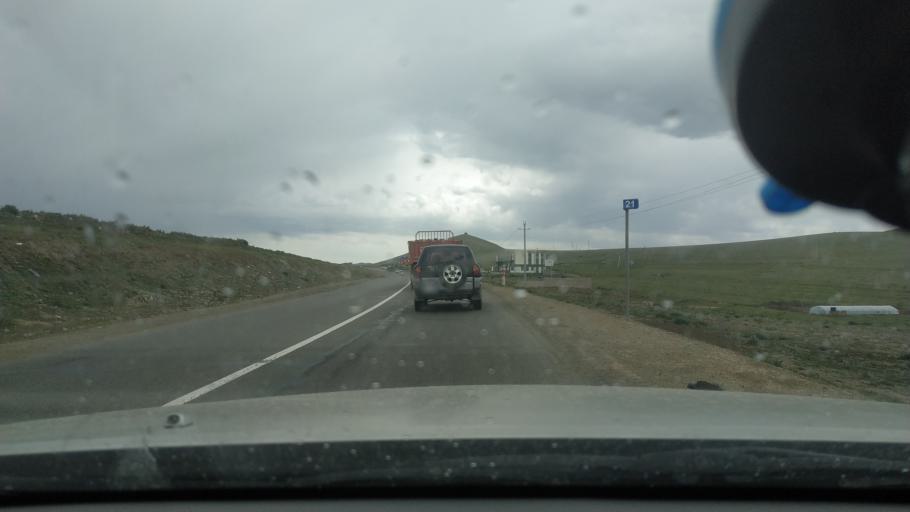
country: MN
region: Ulaanbaatar
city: Ulaanbaatar
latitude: 47.7932
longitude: 106.7451
